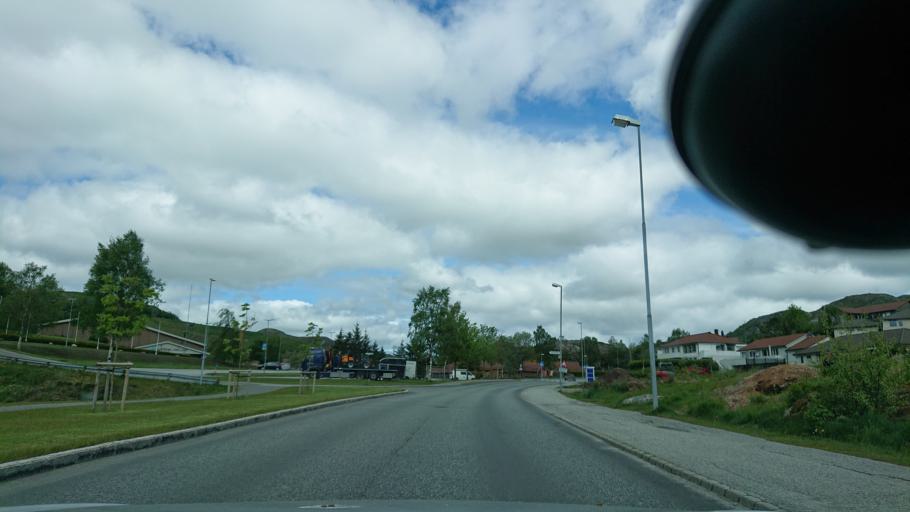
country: NO
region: Rogaland
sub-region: Gjesdal
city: Algard
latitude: 58.7715
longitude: 5.8650
